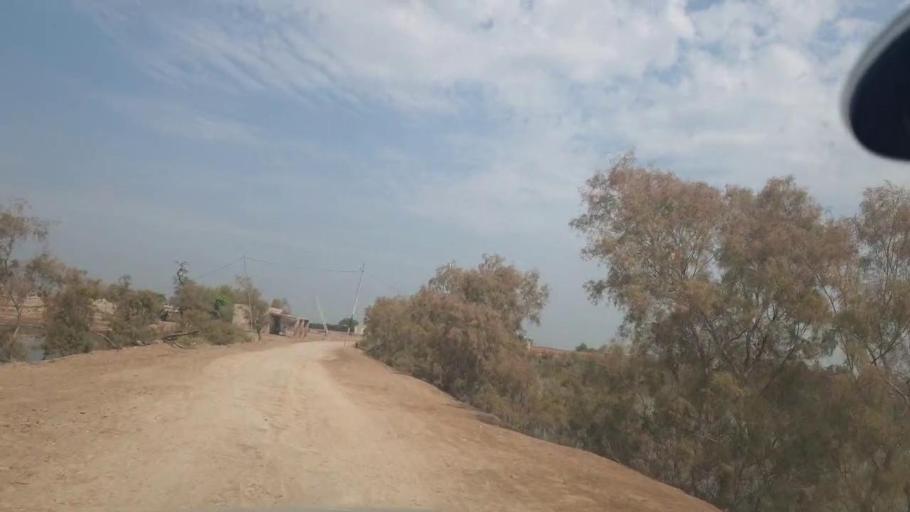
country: PK
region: Balochistan
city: Mehrabpur
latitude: 28.1282
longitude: 68.0882
